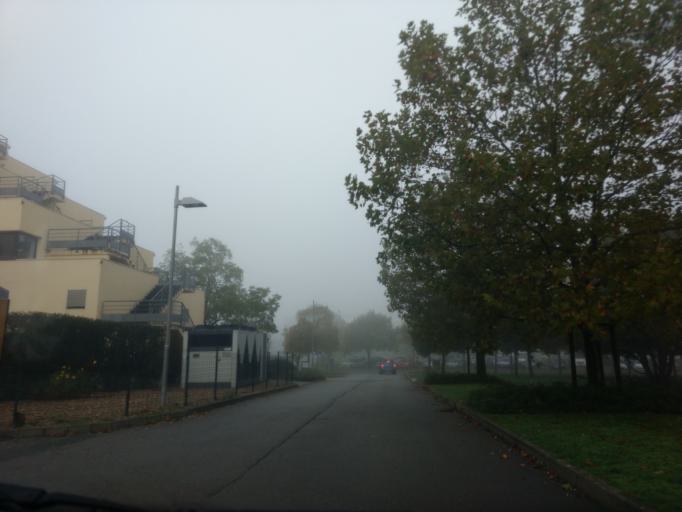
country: FR
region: Poitou-Charentes
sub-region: Departement de la Vienne
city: Chasseneuil-du-Poitou
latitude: 46.6588
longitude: 0.3654
